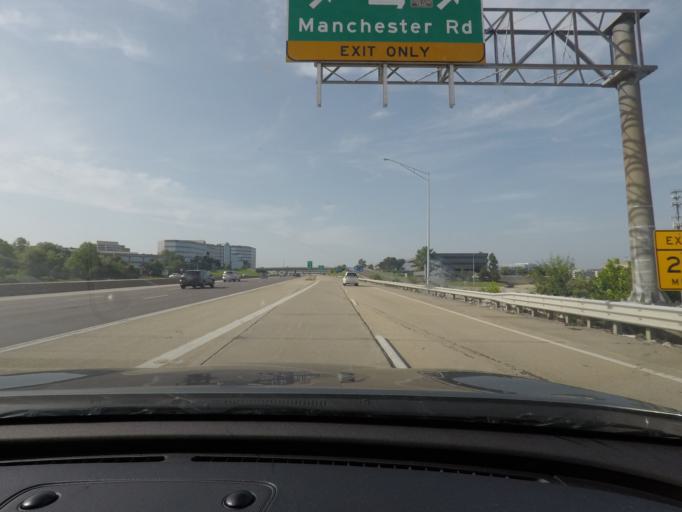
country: US
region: Missouri
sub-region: Saint Louis County
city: Town and Country
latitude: 38.6091
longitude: -90.4515
